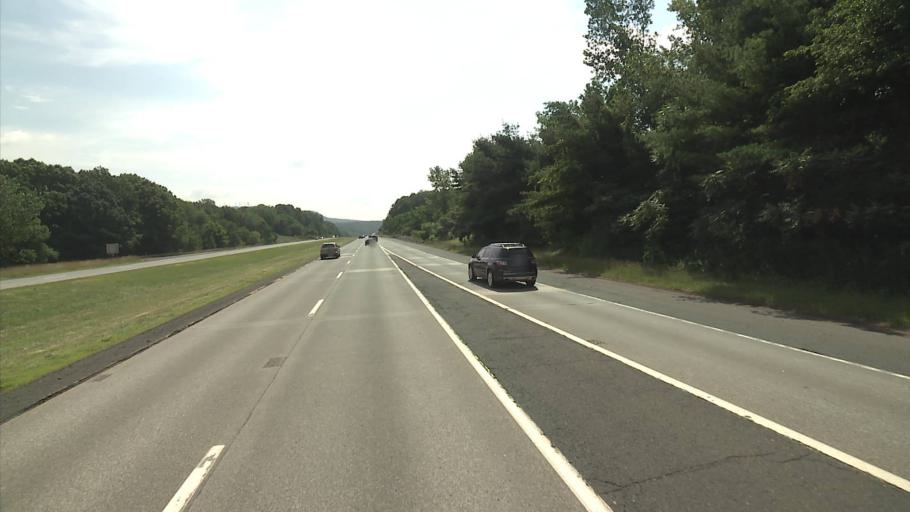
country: US
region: Connecticut
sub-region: New Haven County
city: Cheshire Village
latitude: 41.5566
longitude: -72.8875
